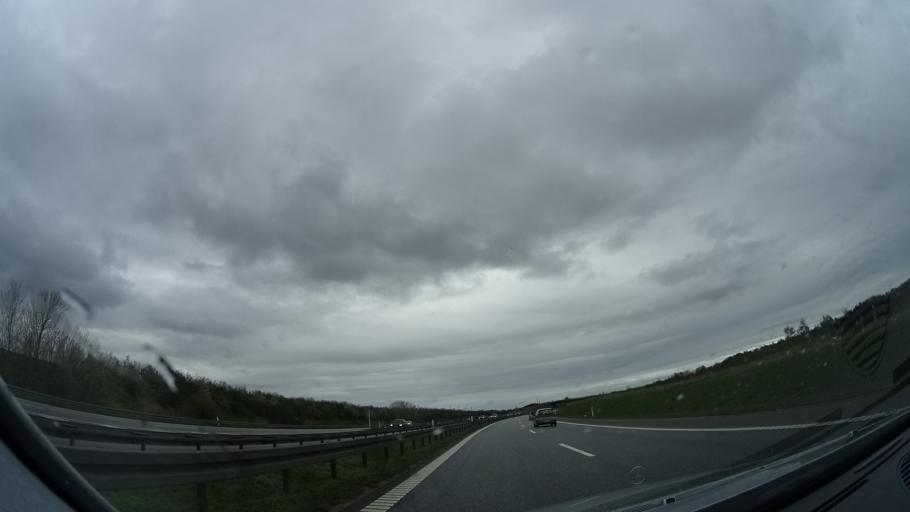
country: DK
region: Capital Region
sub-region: Frederiksberg Kommune
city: Frederiksberg
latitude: 55.6258
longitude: 12.5339
